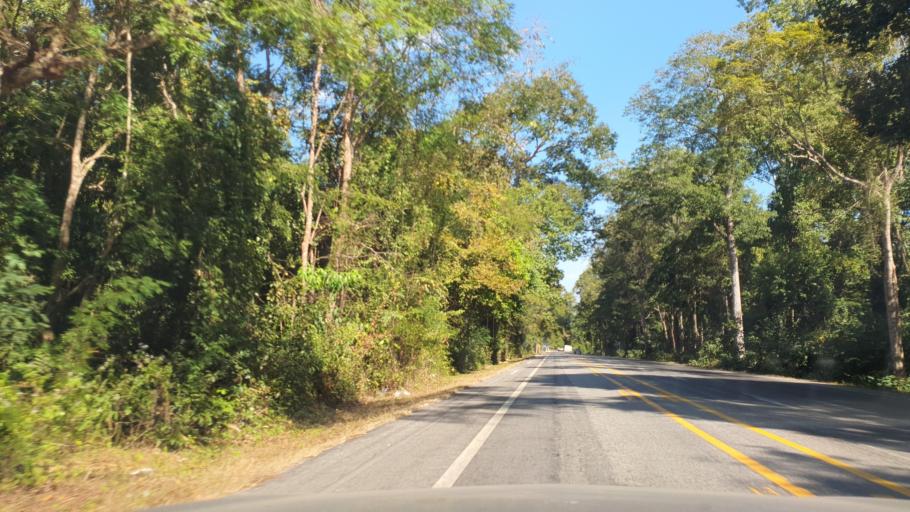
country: TH
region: Kalasin
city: Na Khu
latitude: 16.8442
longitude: 103.9147
